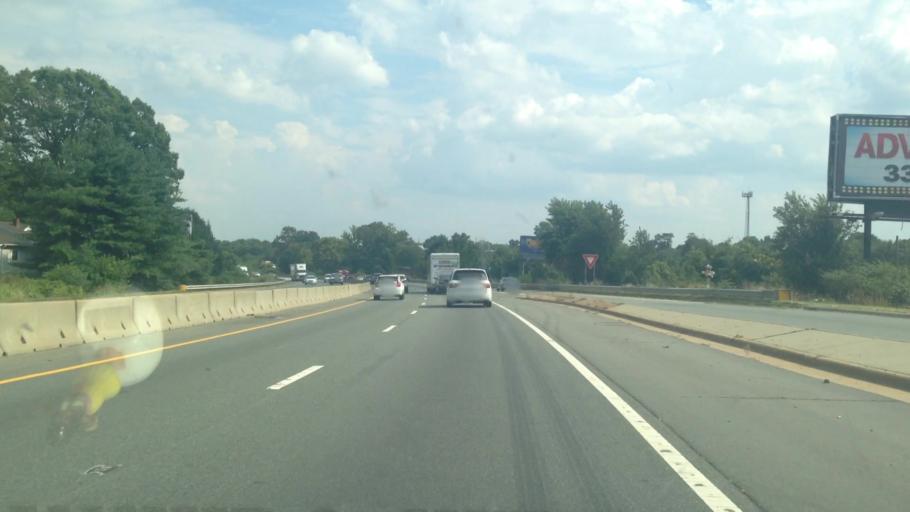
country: US
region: North Carolina
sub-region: Forsyth County
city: Winston-Salem
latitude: 36.1358
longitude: -80.2394
